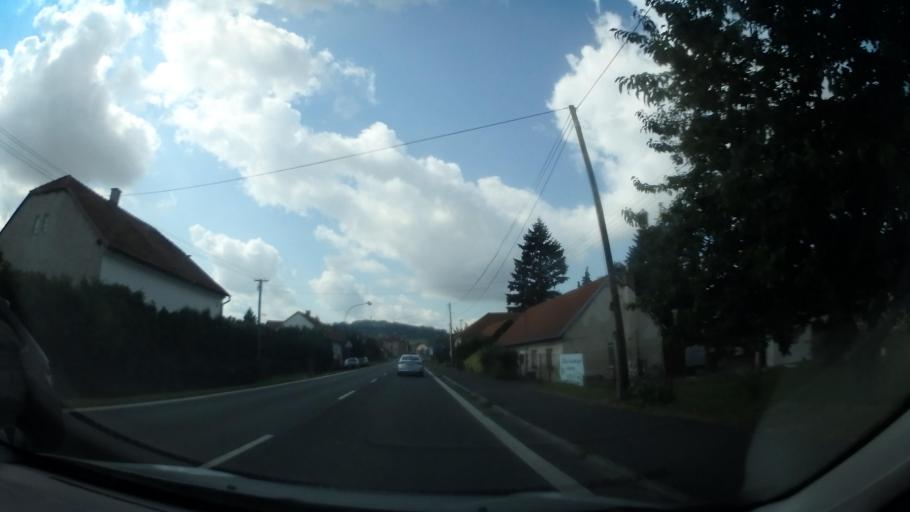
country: CZ
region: Central Bohemia
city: Cervene Pecky
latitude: 49.9470
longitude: 15.2101
